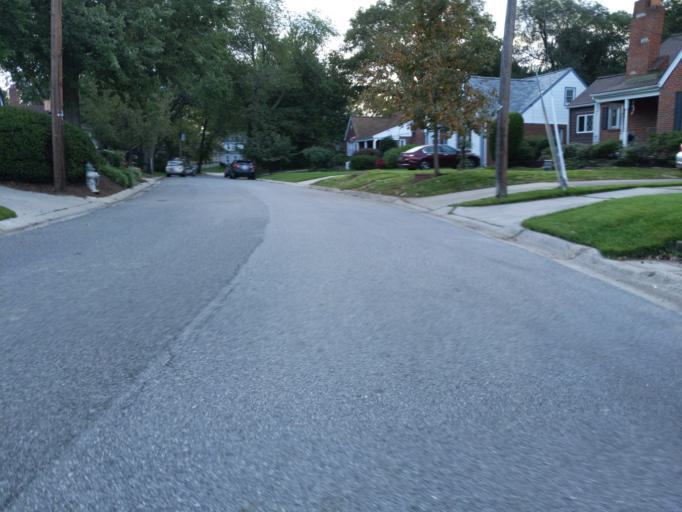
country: US
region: Maryland
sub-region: Montgomery County
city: Forest Glen
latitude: 39.0109
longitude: -77.0454
